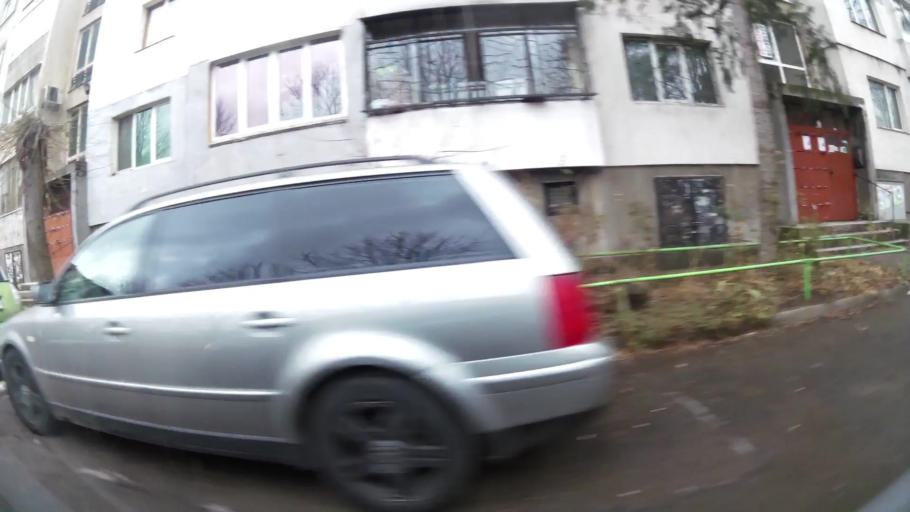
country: BG
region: Sofia-Capital
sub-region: Stolichna Obshtina
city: Sofia
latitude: 42.7240
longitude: 23.2946
